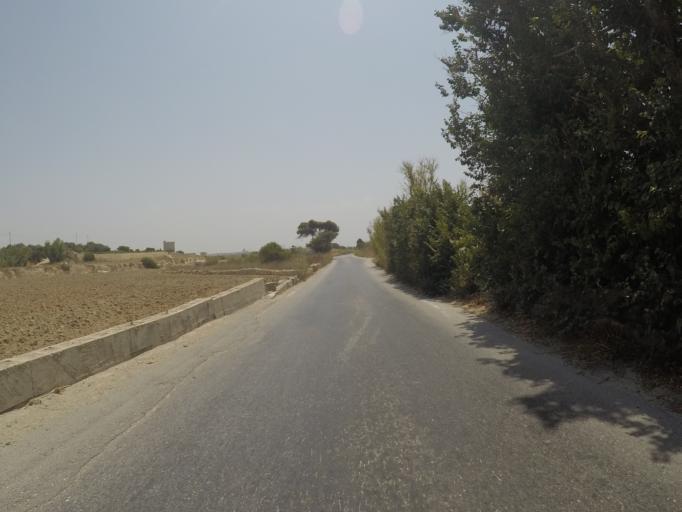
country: MT
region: Ir-Rabat
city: Rabat
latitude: 35.8694
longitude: 14.4147
